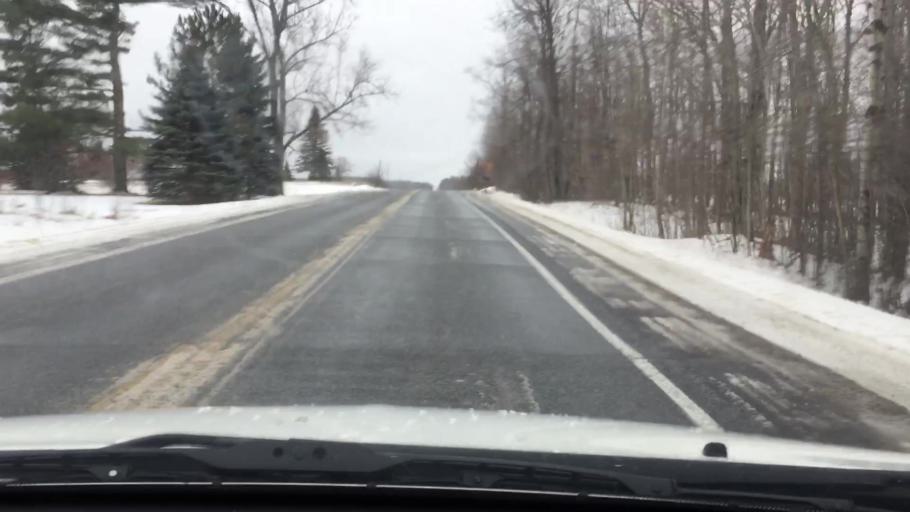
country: US
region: Michigan
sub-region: Wexford County
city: Cadillac
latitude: 44.1102
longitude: -85.4443
